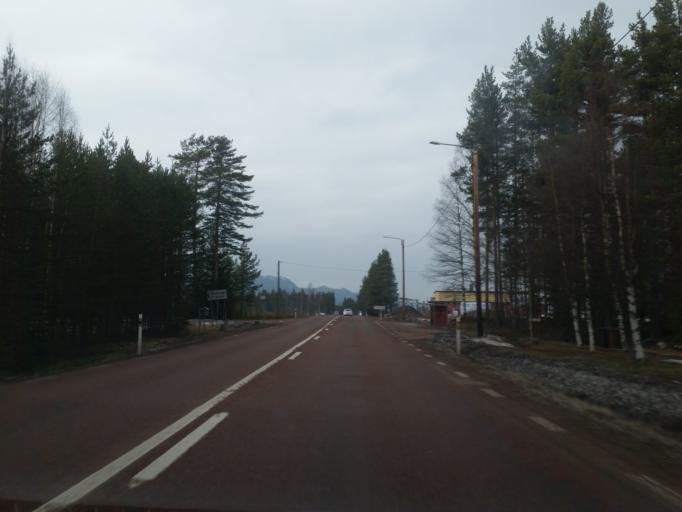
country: SE
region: Dalarna
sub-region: Alvdalens Kommun
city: AElvdalen
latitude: 61.1478
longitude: 14.1478
